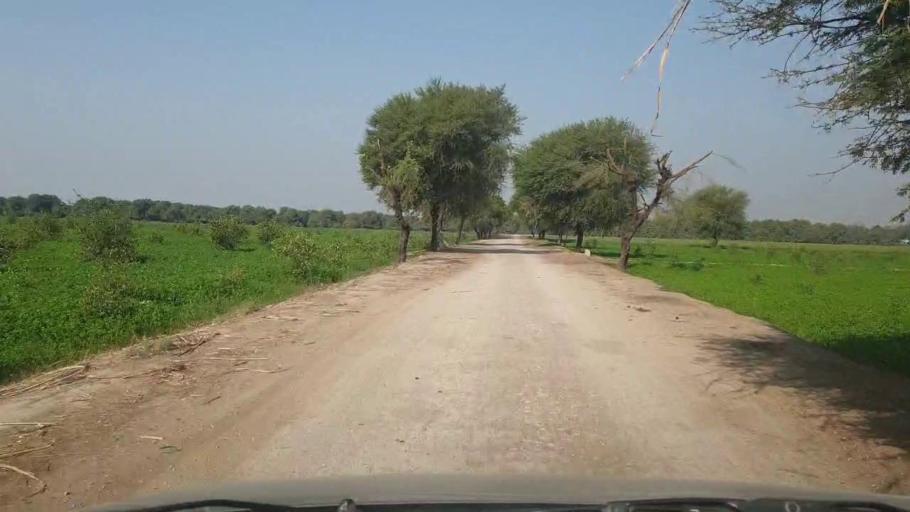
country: PK
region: Sindh
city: Mirwah Gorchani
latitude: 25.2559
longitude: 69.0935
